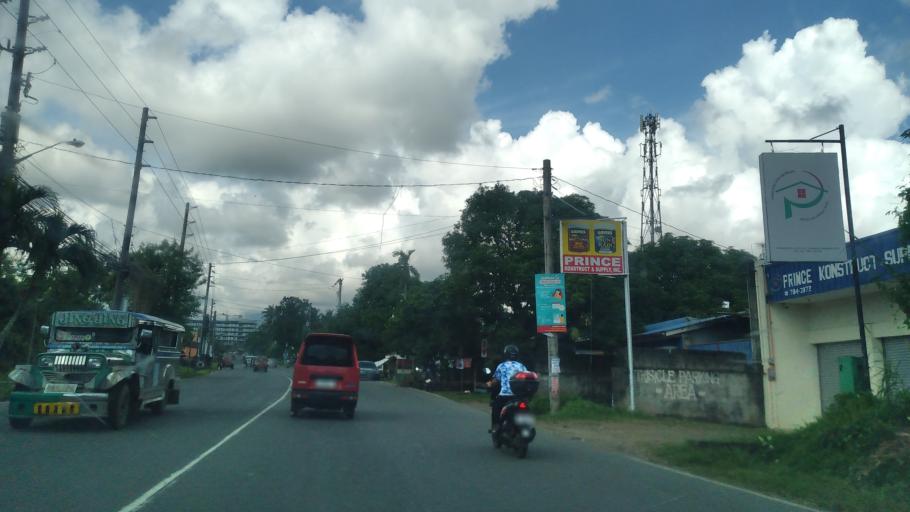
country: PH
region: Calabarzon
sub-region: Province of Quezon
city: Isabang
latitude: 13.9581
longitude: 121.5698
